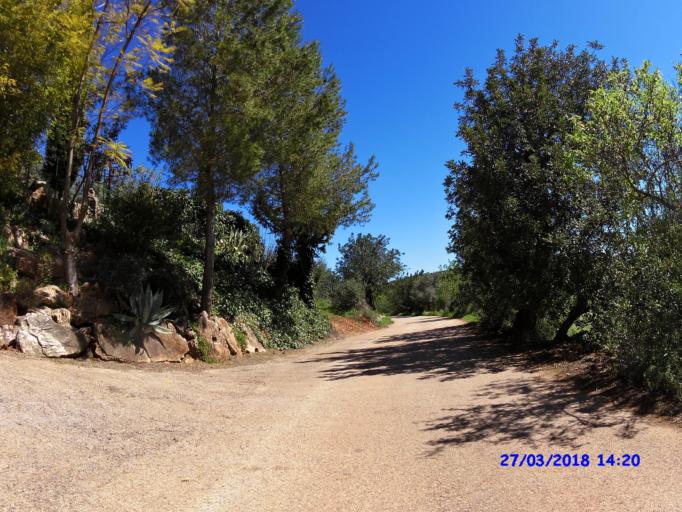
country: PT
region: Faro
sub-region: Loule
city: Boliqueime
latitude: 37.2070
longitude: -8.1666
